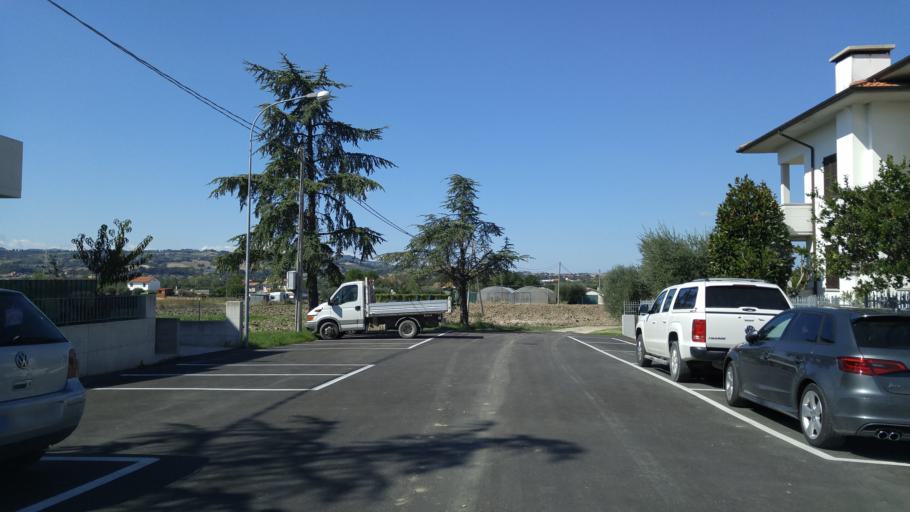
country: IT
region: The Marches
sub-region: Provincia di Pesaro e Urbino
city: Montemaggiore al Metauro
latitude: 43.7498
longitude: 12.9493
